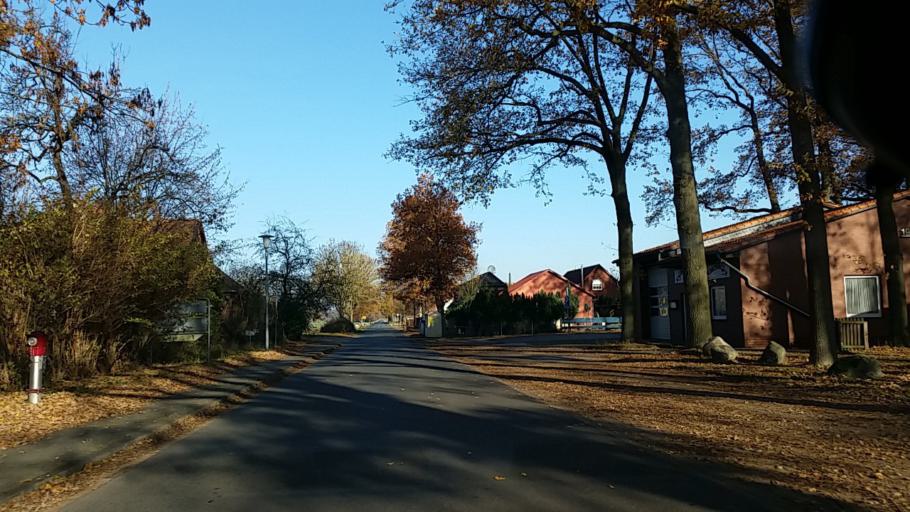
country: DE
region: Lower Saxony
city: Bergfeld
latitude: 52.5463
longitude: 10.8496
